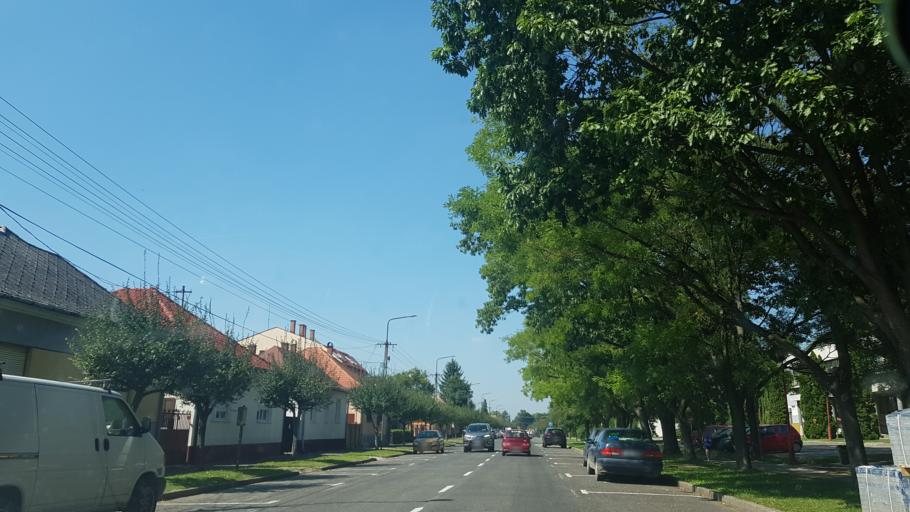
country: HU
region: Somogy
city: Nagyatad
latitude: 46.2318
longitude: 17.3610
